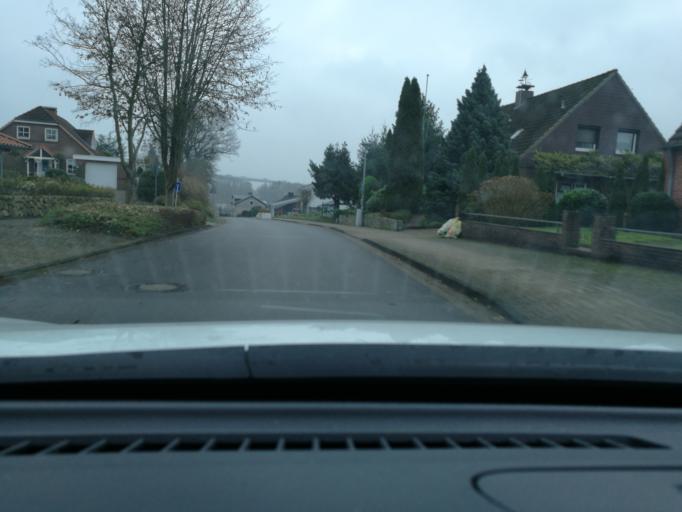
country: DE
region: Schleswig-Holstein
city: Borgstedt
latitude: 54.3301
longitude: 9.7100
